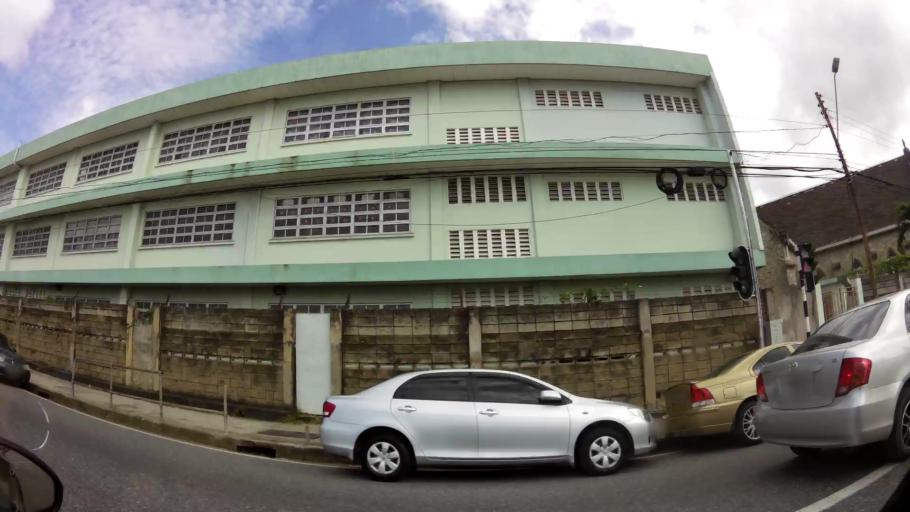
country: TT
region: City of Port of Spain
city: Port-of-Spain
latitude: 10.6596
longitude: -61.5157
